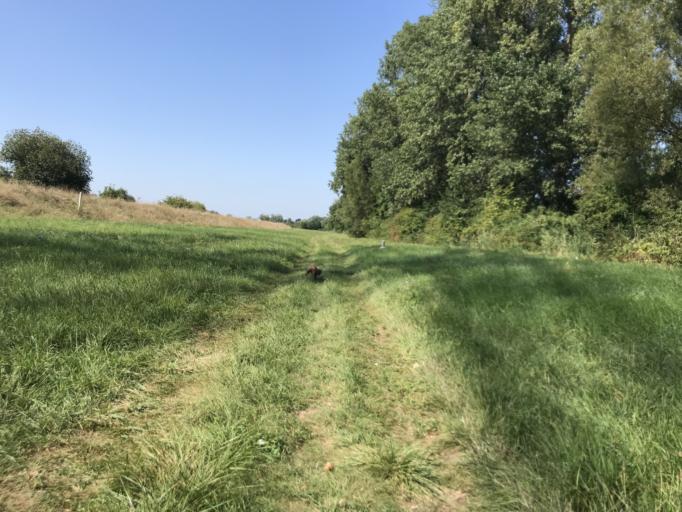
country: DE
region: Hesse
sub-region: Regierungsbezirk Darmstadt
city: Bischofsheim
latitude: 49.9993
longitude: 8.3812
